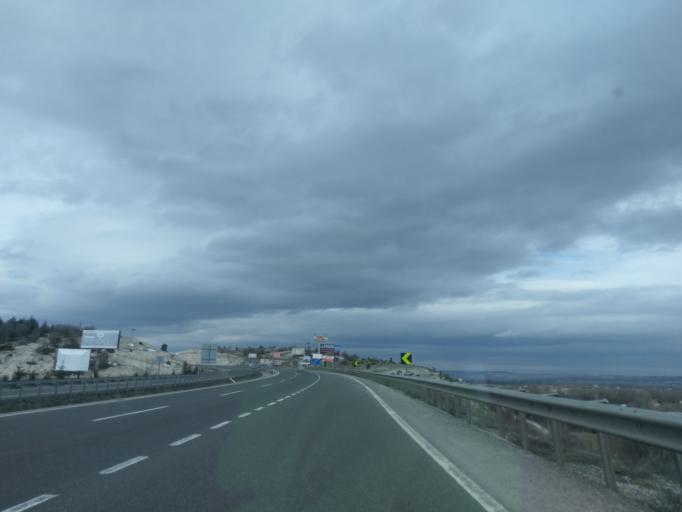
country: TR
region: Kuetahya
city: Kutahya
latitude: 39.3719
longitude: 30.0665
